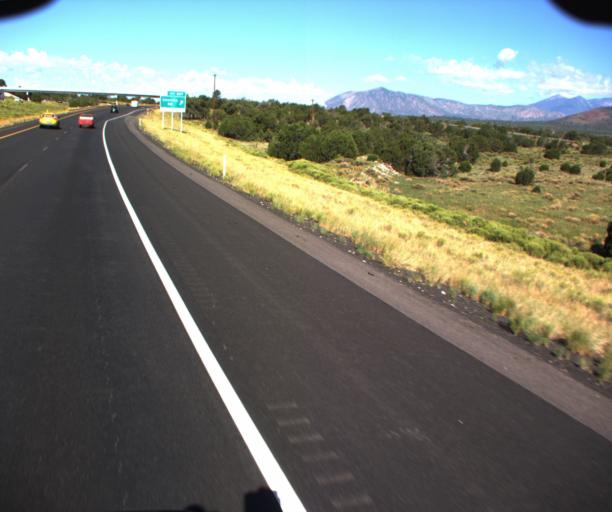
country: US
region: Arizona
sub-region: Coconino County
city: Flagstaff
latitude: 35.2020
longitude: -111.4727
